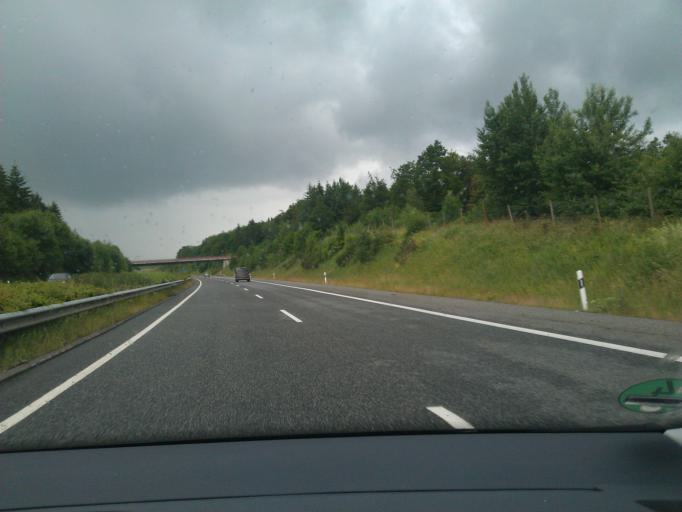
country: DE
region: Rheinland-Pfalz
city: Gindorf
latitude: 50.0191
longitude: 6.6598
